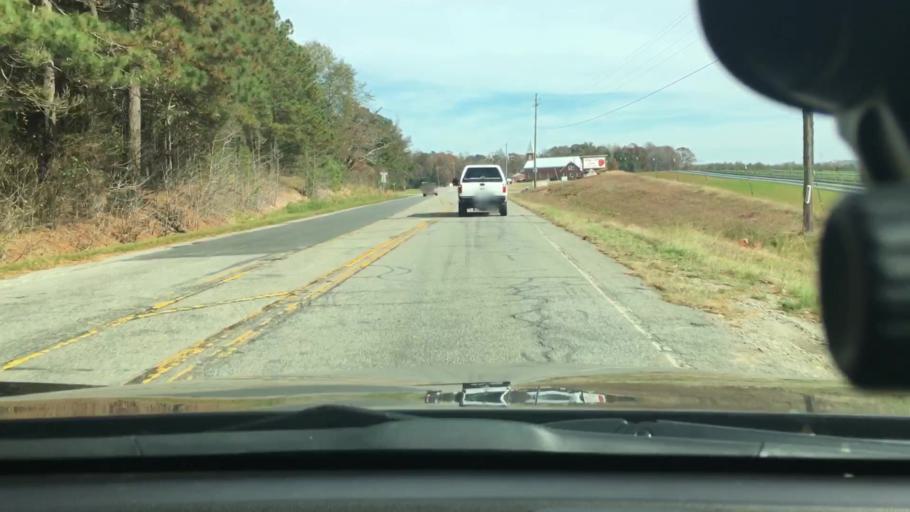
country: US
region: North Carolina
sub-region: Moore County
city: Carthage
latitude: 35.3808
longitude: -79.2819
